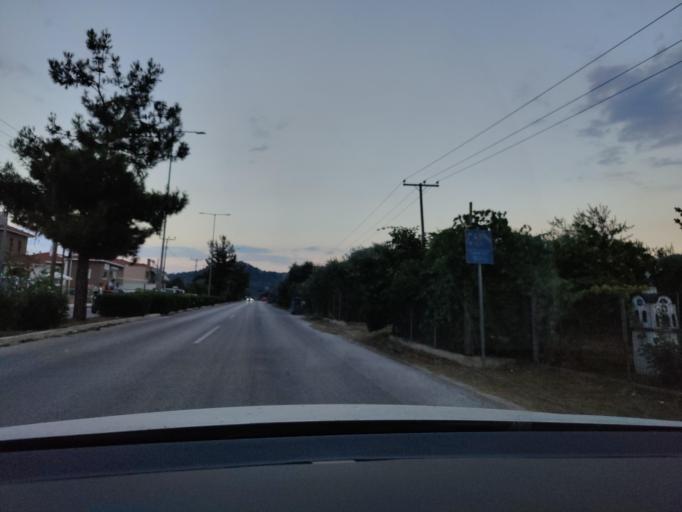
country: GR
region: East Macedonia and Thrace
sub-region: Nomos Kavalas
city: Thasos
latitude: 40.7731
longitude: 24.6962
